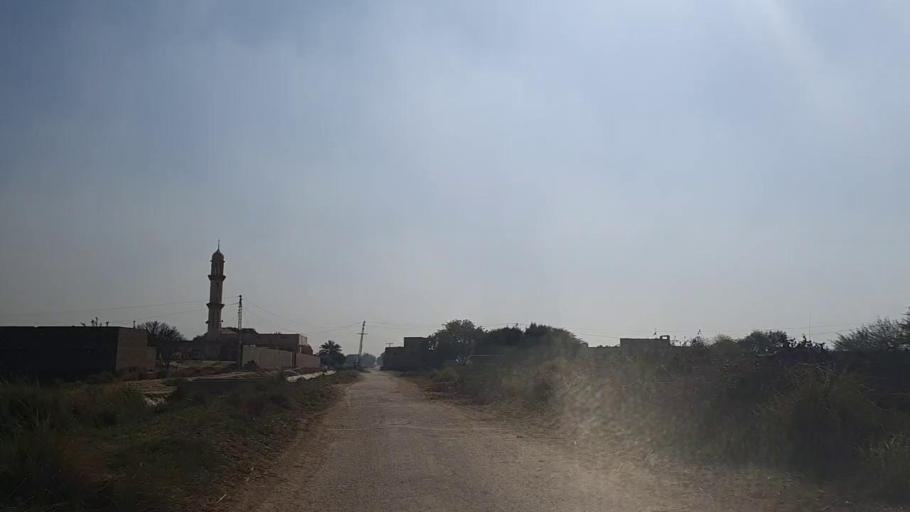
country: PK
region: Sindh
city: Shahpur Chakar
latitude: 26.1899
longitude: 68.5835
